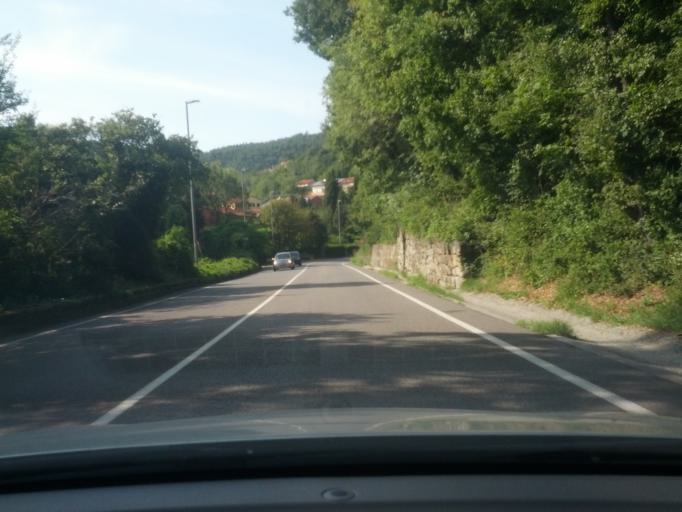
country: IT
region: Friuli Venezia Giulia
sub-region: Provincia di Trieste
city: Trieste
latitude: 45.6621
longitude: 13.8048
